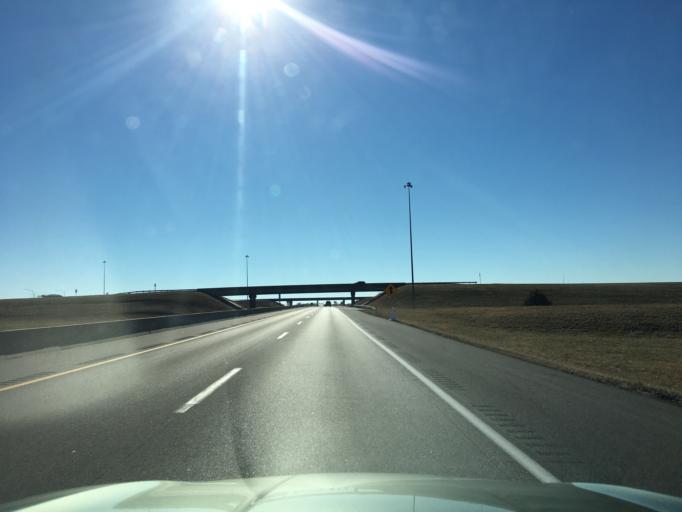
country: US
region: Kansas
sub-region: Sumner County
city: Wellington
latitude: 37.2805
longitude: -97.3404
